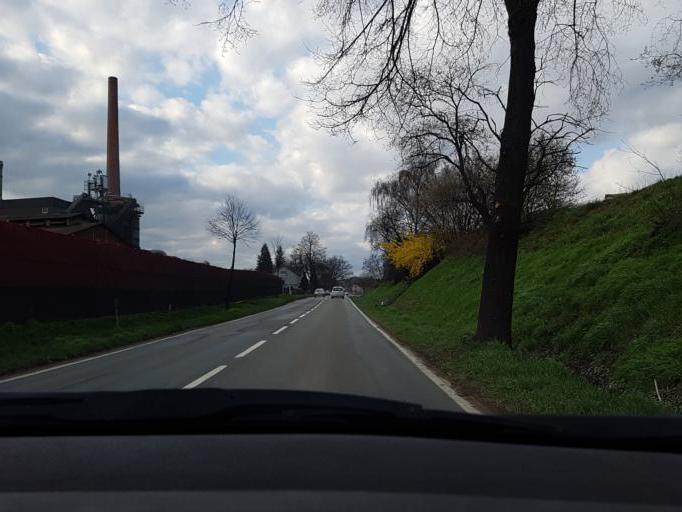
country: DE
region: Lower Saxony
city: Bodenfelde
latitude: 51.6311
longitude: 9.5625
